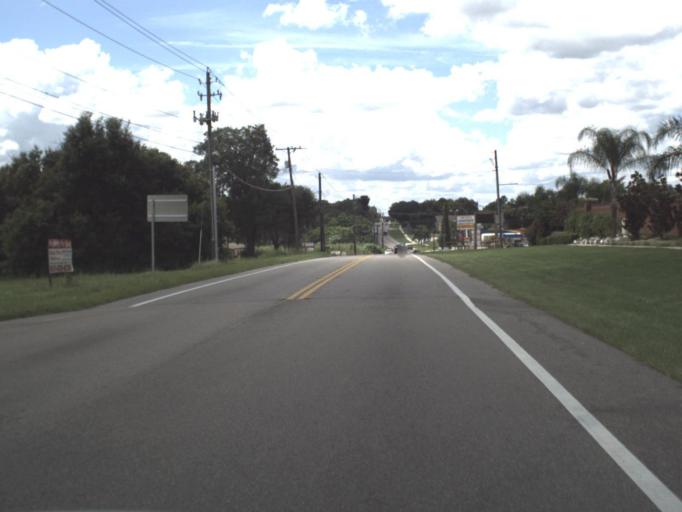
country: US
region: Florida
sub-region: Polk County
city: Cypress Gardens
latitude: 28.0225
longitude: -81.6969
